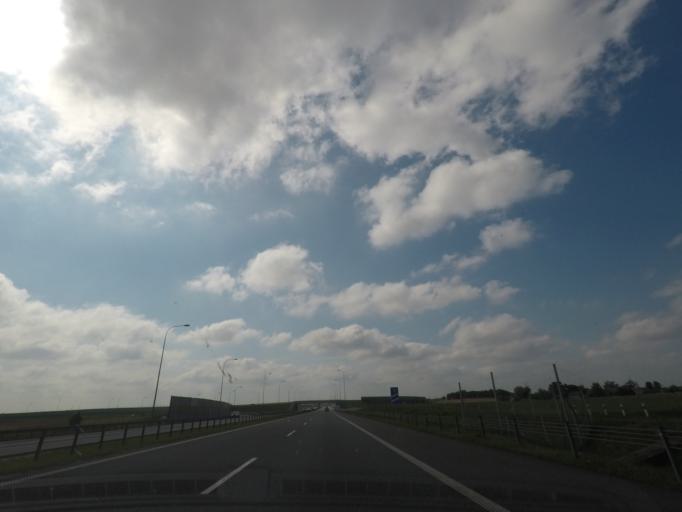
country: PL
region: Kujawsko-Pomorskie
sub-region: Powiat torunski
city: Lubicz Dolny
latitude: 53.0941
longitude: 18.7496
